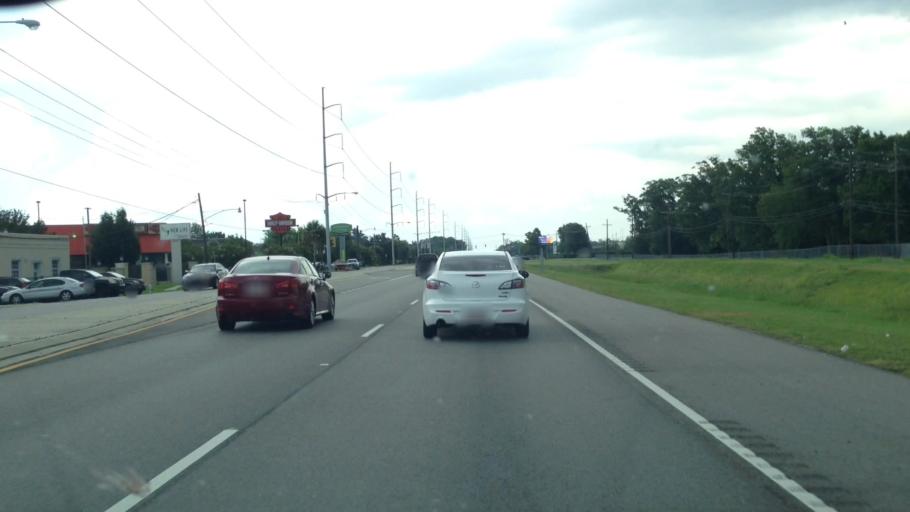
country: US
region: Louisiana
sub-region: Jefferson Parish
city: River Ridge
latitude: 29.9770
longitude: -90.2002
